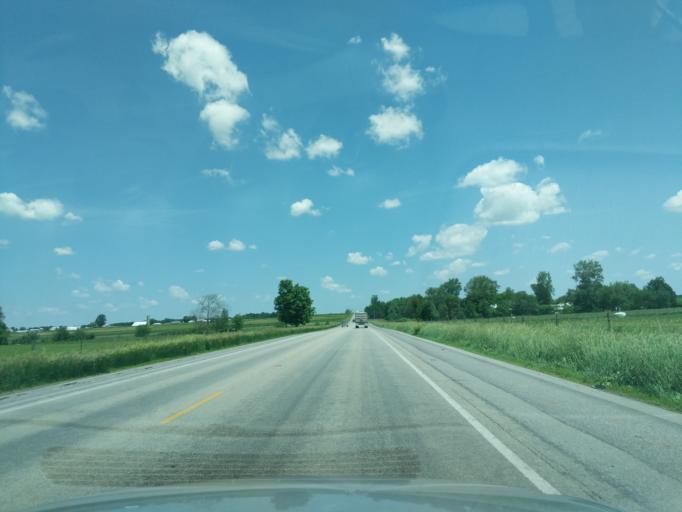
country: US
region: Indiana
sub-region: LaGrange County
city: Topeka
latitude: 41.6160
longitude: -85.5796
